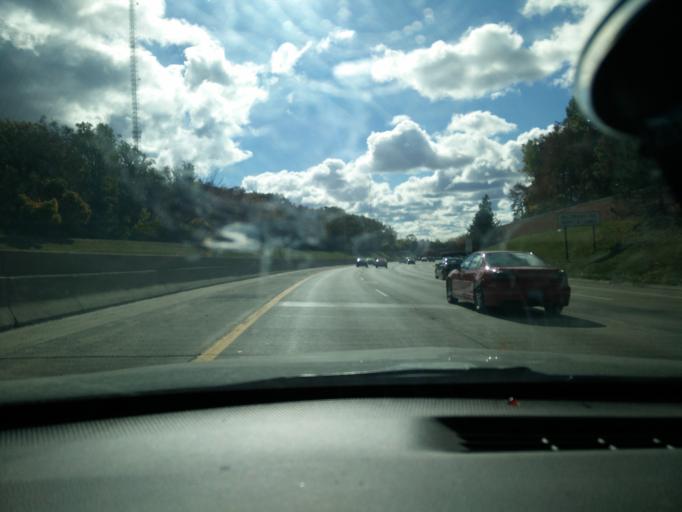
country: US
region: Michigan
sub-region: Oakland County
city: Southfield
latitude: 42.4854
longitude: -83.2088
